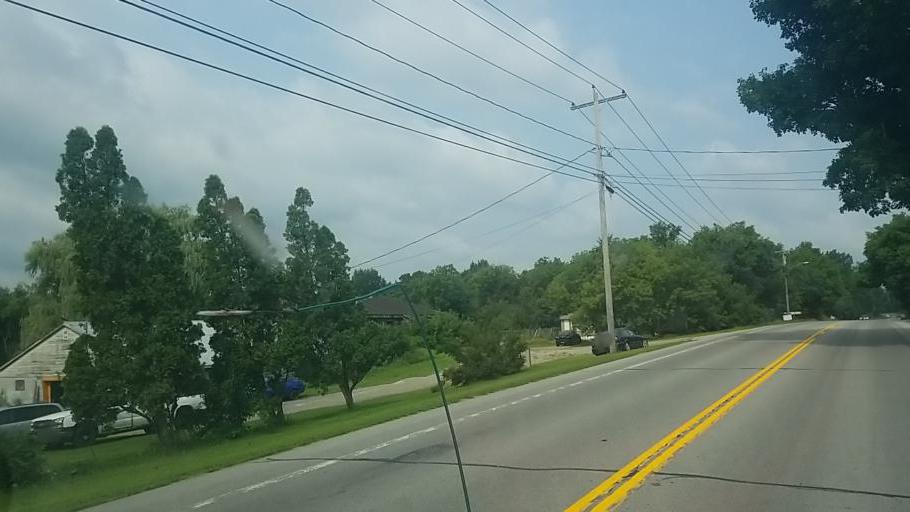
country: US
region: New York
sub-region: Montgomery County
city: Fort Plain
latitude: 42.9224
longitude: -74.5999
